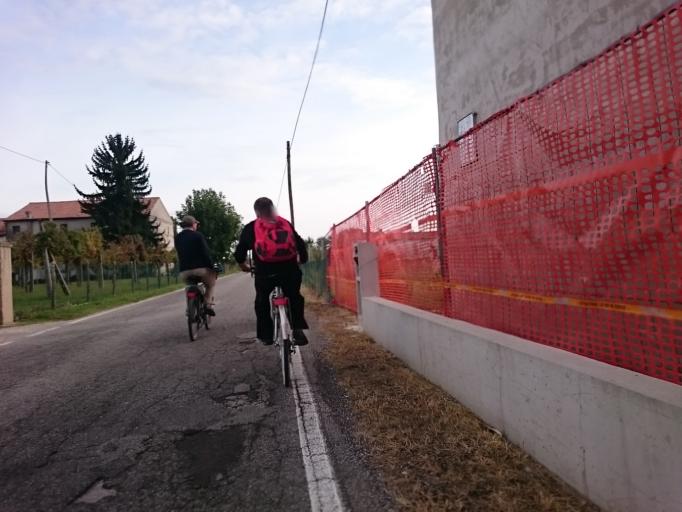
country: IT
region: Veneto
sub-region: Provincia di Vicenza
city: Grumolo delle Abbadesse
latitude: 45.5459
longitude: 11.6825
